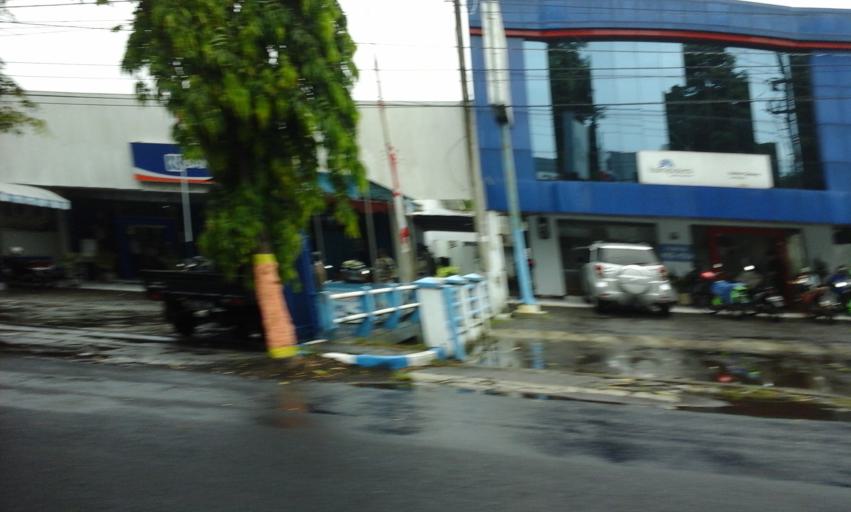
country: ID
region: East Java
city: Rogotrunan
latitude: -8.1238
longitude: 113.2272
